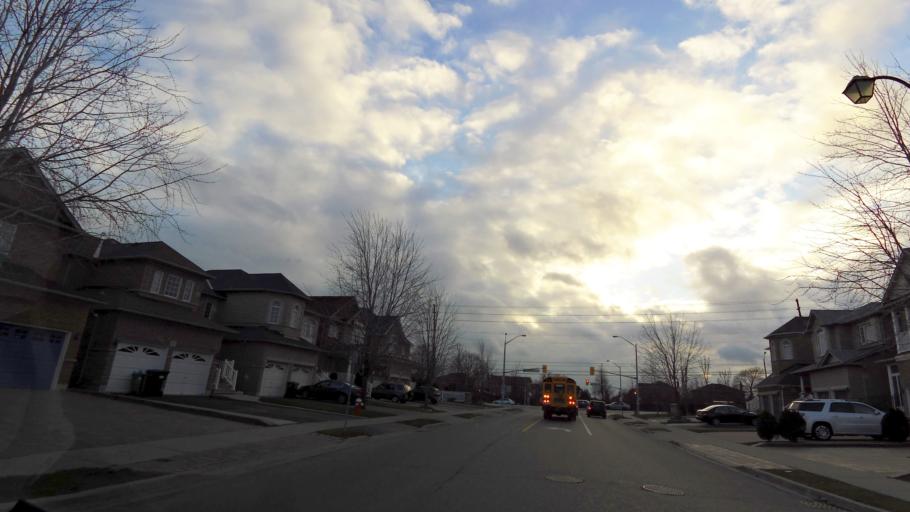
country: CA
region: Ontario
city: Brampton
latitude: 43.7527
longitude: -79.7300
